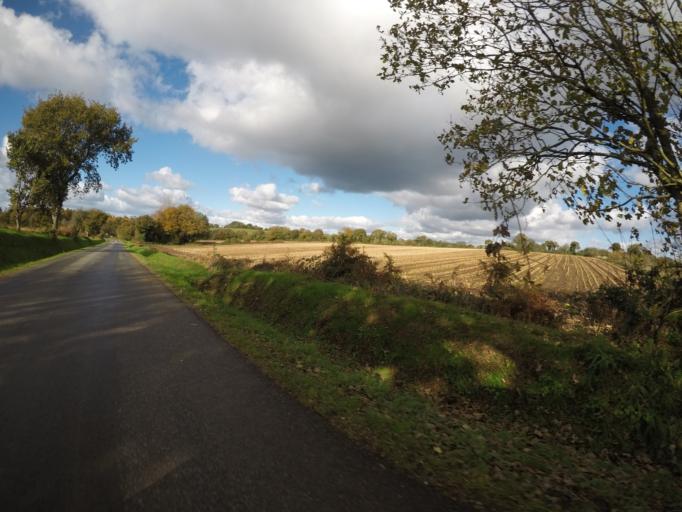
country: FR
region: Brittany
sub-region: Departement des Cotes-d'Armor
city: Bourbriac
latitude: 48.4601
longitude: -3.2957
